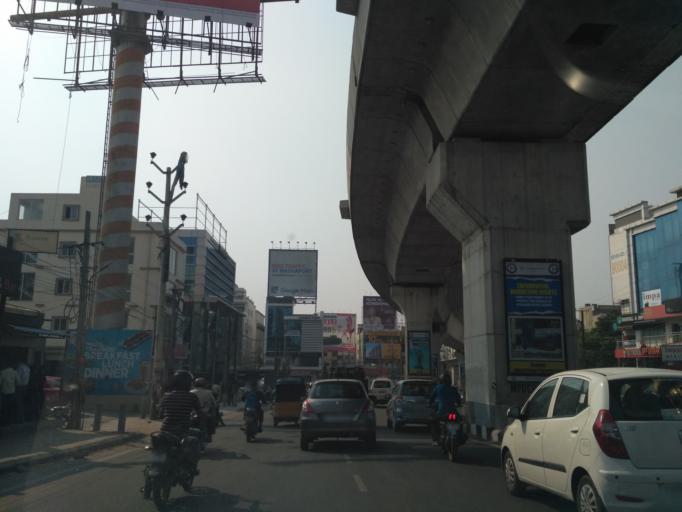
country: IN
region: Telangana
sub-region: Rangareddi
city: Kukatpalli
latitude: 17.4389
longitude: 78.3970
